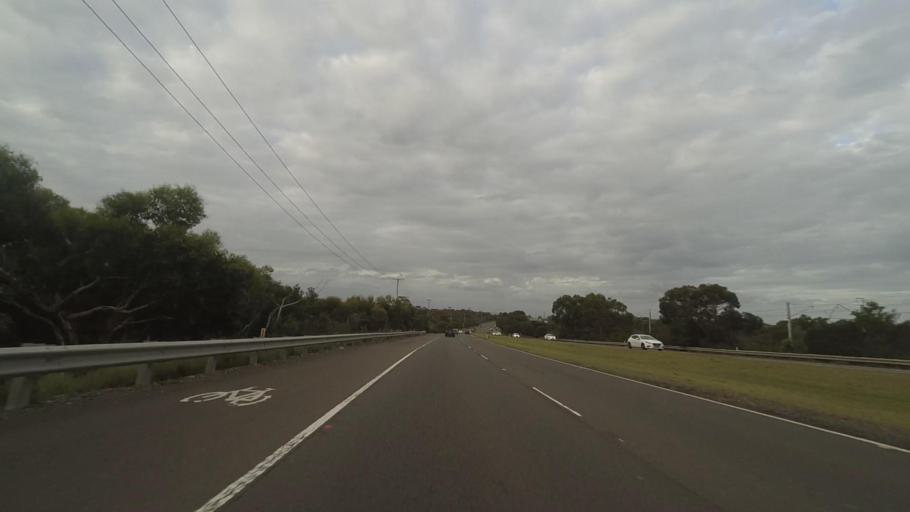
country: AU
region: New South Wales
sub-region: Sutherland Shire
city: Heathcote
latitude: -34.1046
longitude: 150.9937
